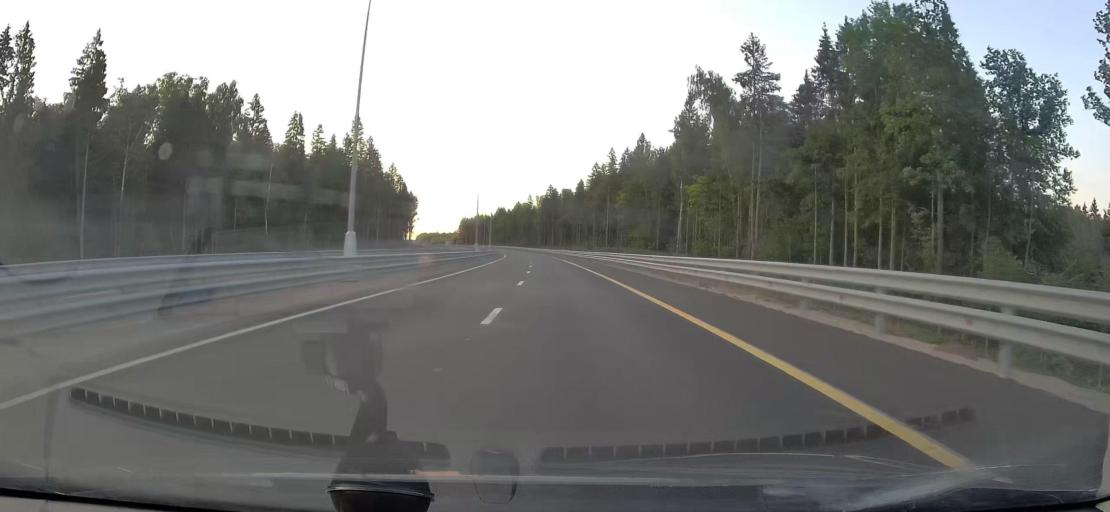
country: RU
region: Moskovskaya
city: Aprelevka
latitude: 55.4321
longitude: 37.1647
